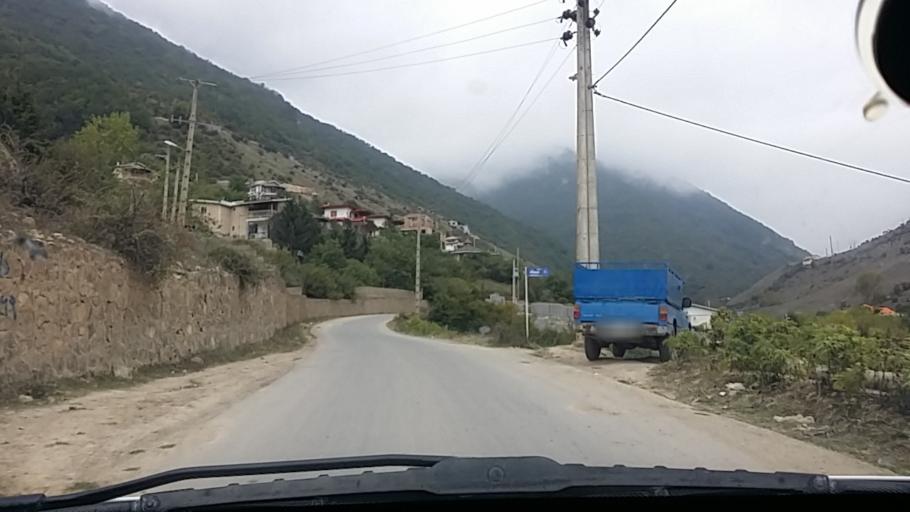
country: IR
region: Mazandaran
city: `Abbasabad
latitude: 36.4747
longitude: 51.1401
